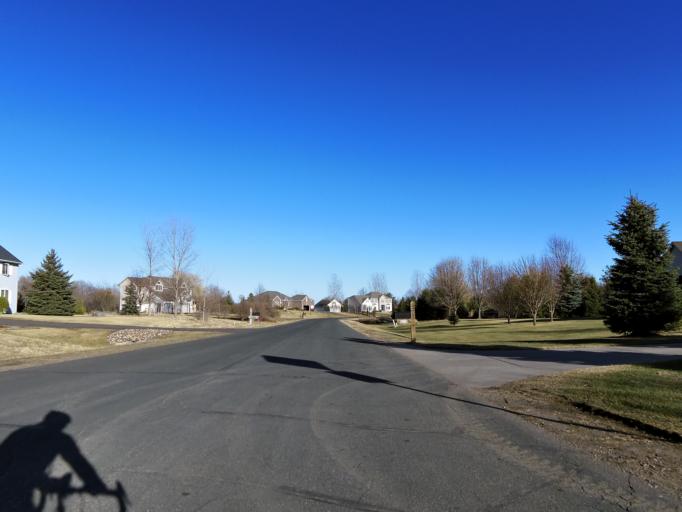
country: US
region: Wisconsin
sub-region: Saint Croix County
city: North Hudson
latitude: 44.9844
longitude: -92.7899
